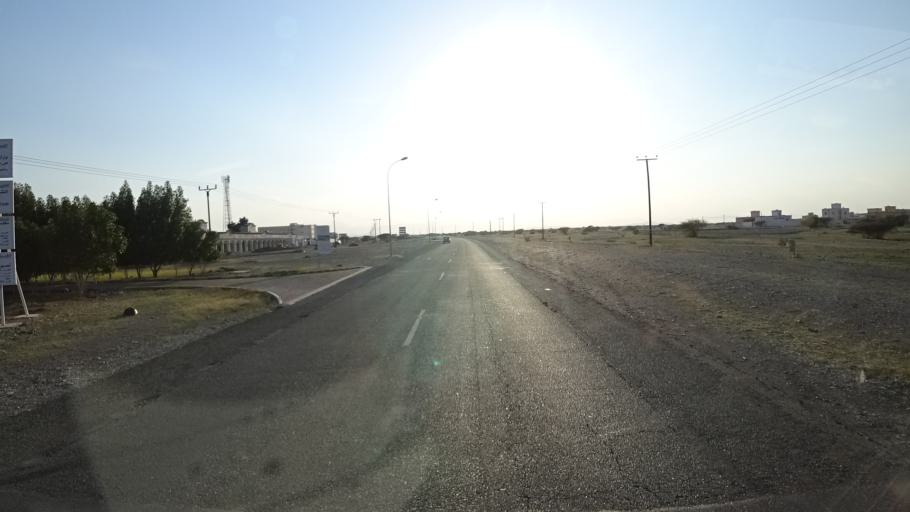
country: OM
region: Al Batinah
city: Al Khaburah
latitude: 23.9474
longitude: 57.0522
